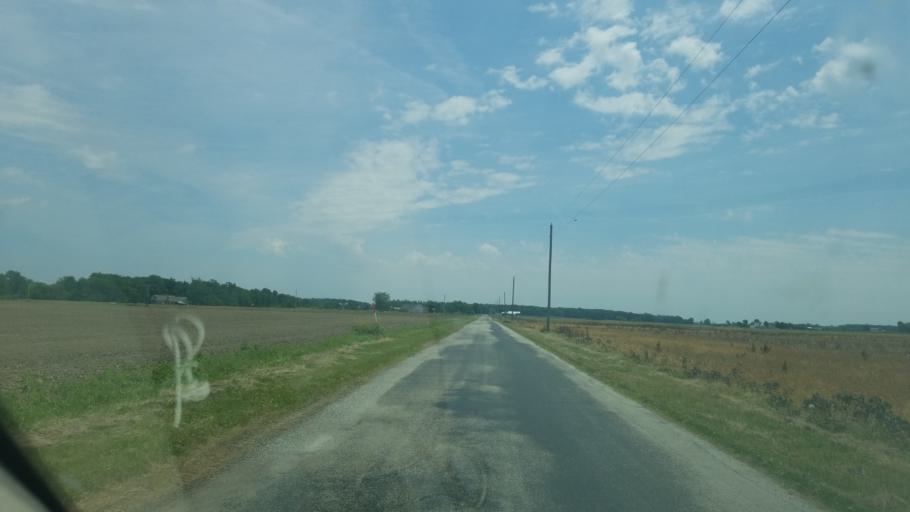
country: US
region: Ohio
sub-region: Wood County
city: North Baltimore
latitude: 41.2220
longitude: -83.6061
